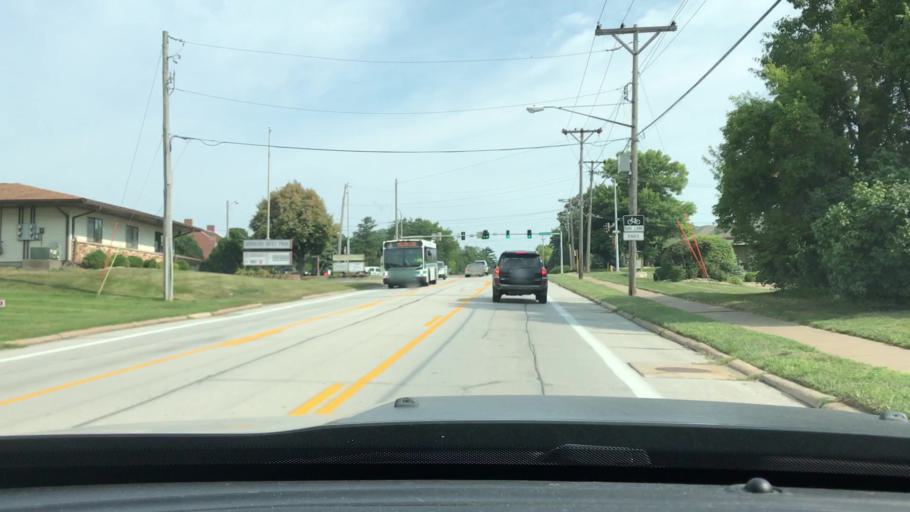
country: US
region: Iowa
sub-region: Scott County
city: Bettendorf
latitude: 41.5557
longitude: -90.5417
